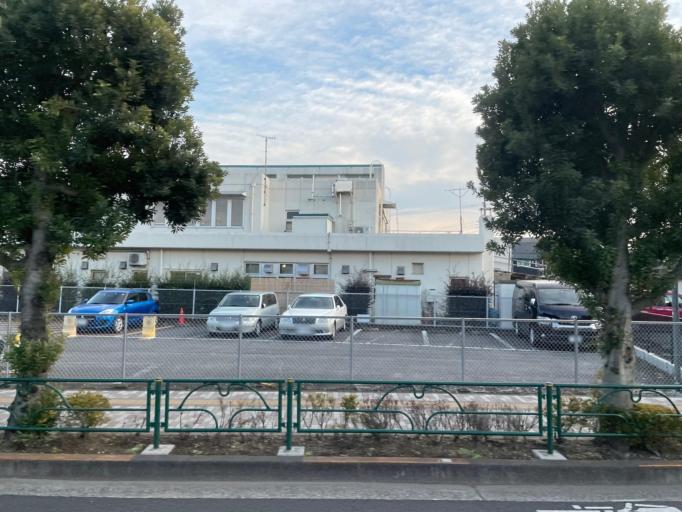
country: JP
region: Tokyo
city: Tanashicho
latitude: 35.7570
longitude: 139.5265
